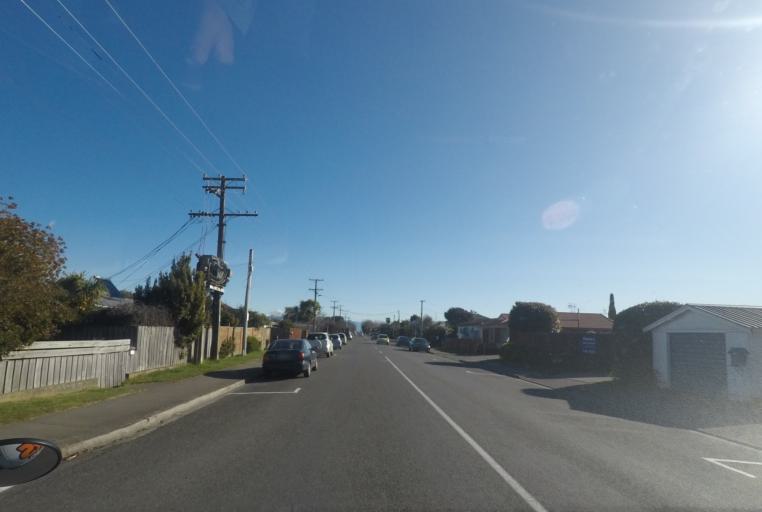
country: NZ
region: Nelson
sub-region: Nelson City
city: Nelson
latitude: -41.2873
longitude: 173.2372
